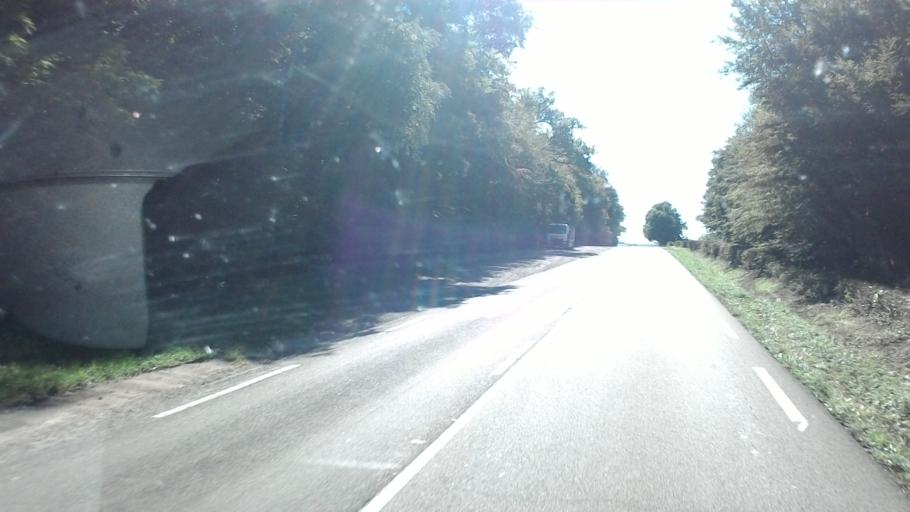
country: FR
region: Bourgogne
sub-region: Departement de la Cote-d'Or
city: Semur-en-Auxois
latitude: 47.4193
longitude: 4.3110
